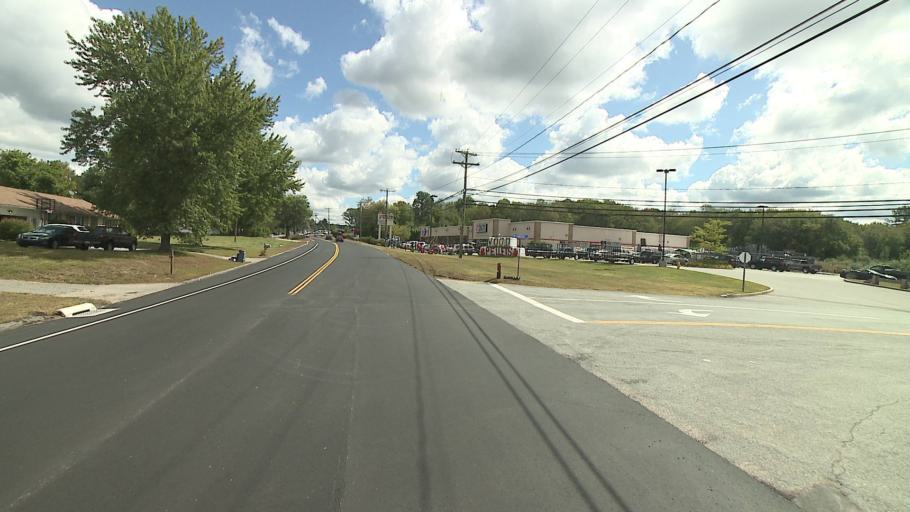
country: US
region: Connecticut
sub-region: Windham County
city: Putnam
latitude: 41.9251
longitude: -71.8752
